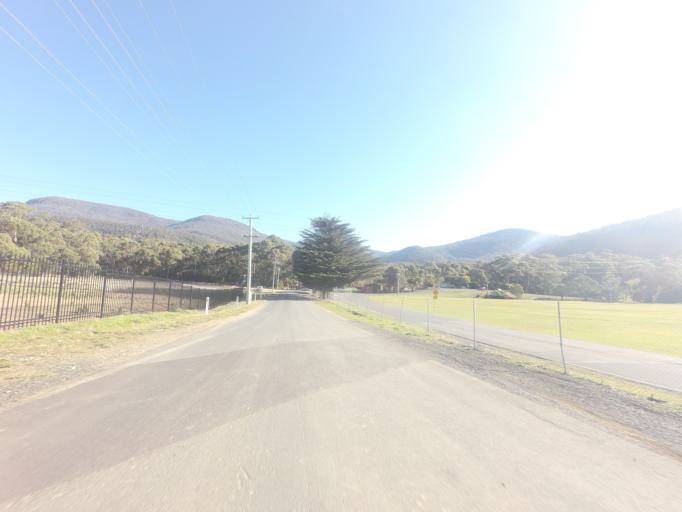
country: AU
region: Tasmania
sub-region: Glenorchy
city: West Moonah
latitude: -42.8535
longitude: 147.2521
